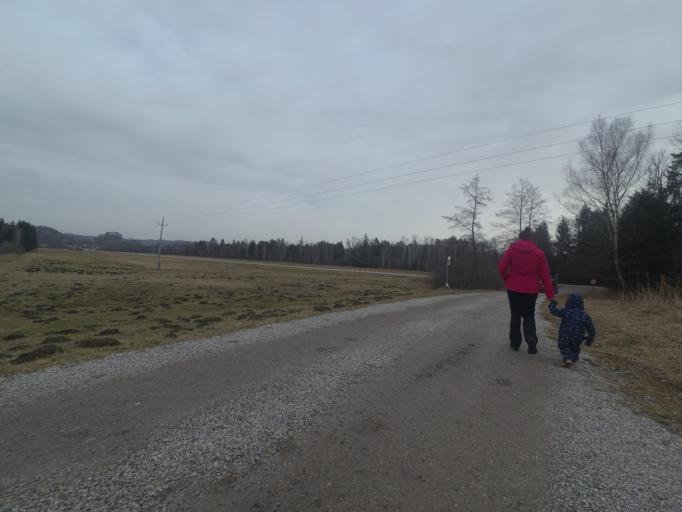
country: AT
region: Salzburg
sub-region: Politischer Bezirk Salzburg-Umgebung
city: Lamprechtshausen
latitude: 48.0537
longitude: 12.9550
